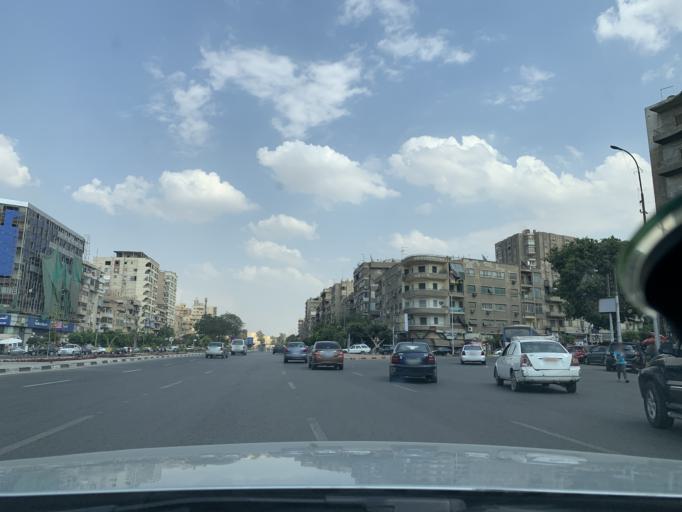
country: EG
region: Muhafazat al Qahirah
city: Cairo
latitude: 30.1055
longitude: 31.3433
